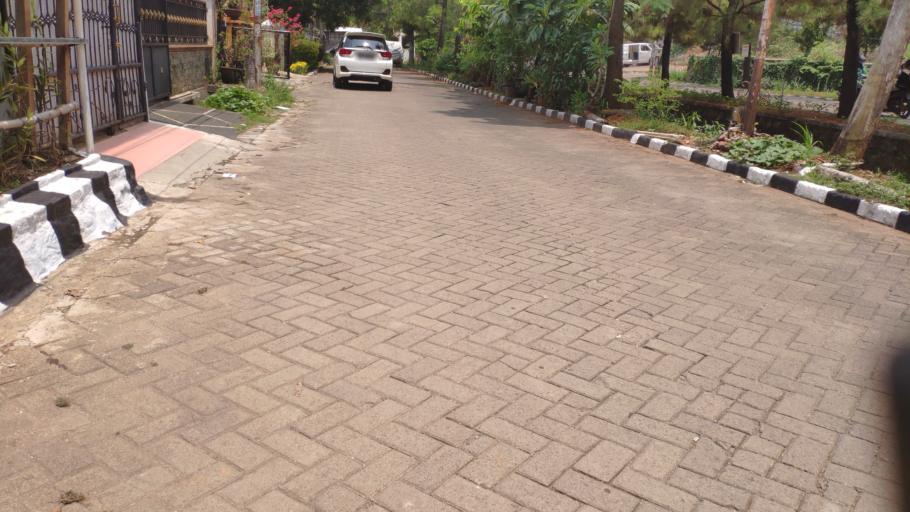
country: ID
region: West Java
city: Sawangan
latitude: -6.3972
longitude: 106.7932
